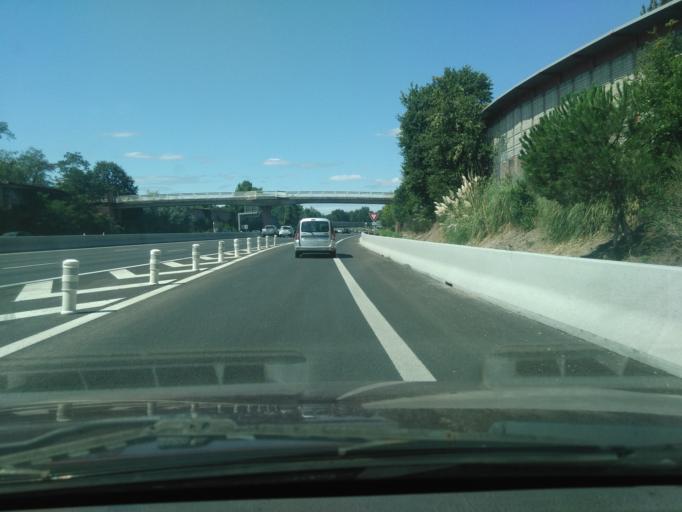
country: FR
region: Aquitaine
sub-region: Departement de la Gironde
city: Pessac
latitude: 44.8055
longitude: -0.6641
